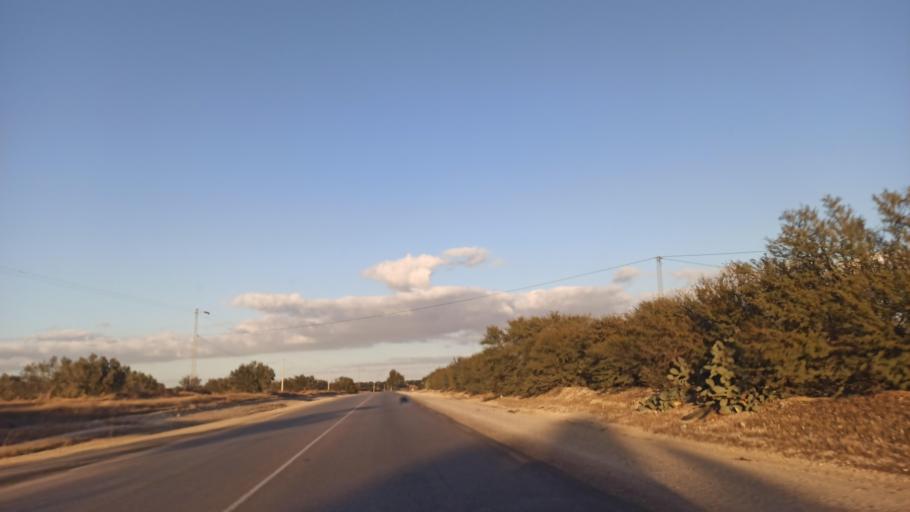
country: TN
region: Al Qayrawan
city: Sbikha
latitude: 35.8743
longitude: 10.2203
